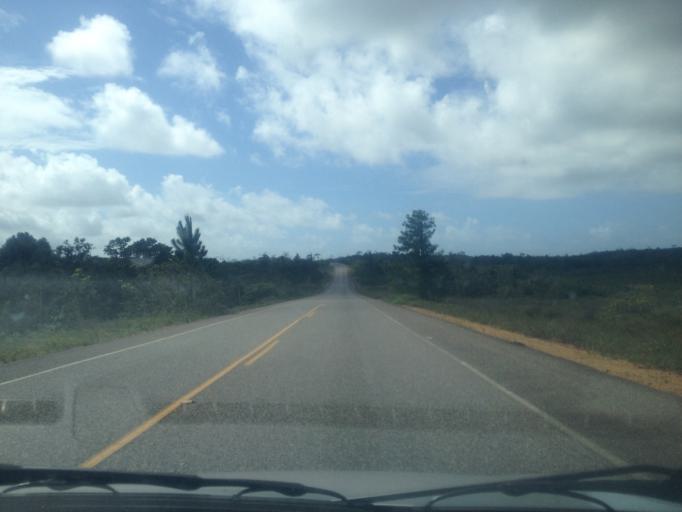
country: BR
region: Bahia
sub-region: Entre Rios
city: Entre Rios
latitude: -12.2425
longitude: -37.8521
